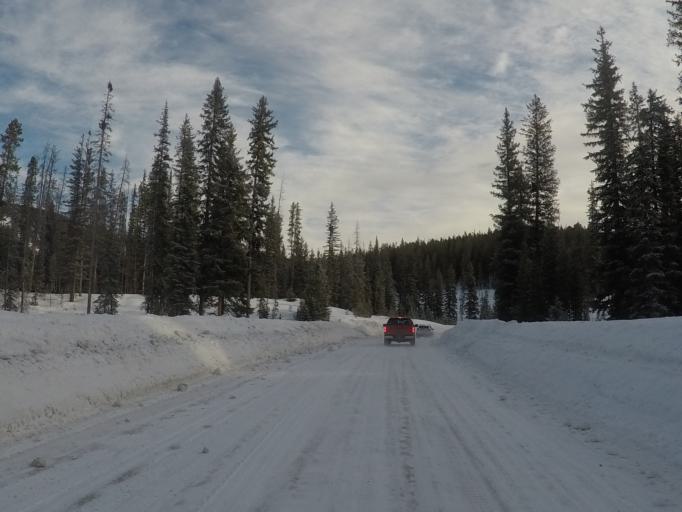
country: US
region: Montana
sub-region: Granite County
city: Philipsburg
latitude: 46.2373
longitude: -113.2448
